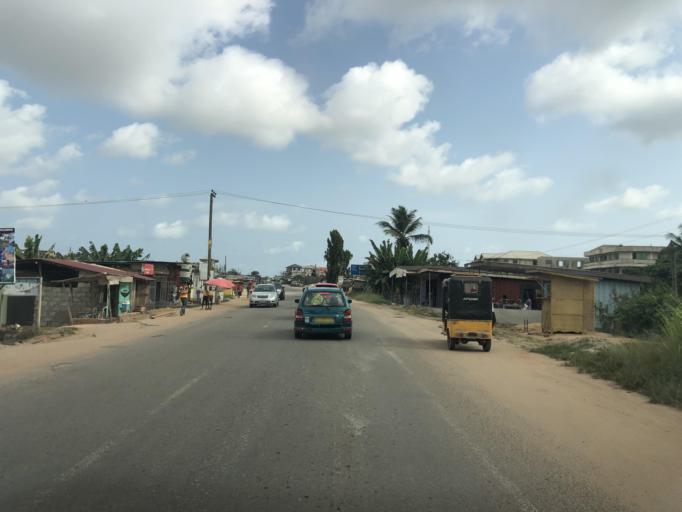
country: GH
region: Central
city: Cape Coast
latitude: 5.1451
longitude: -1.2866
